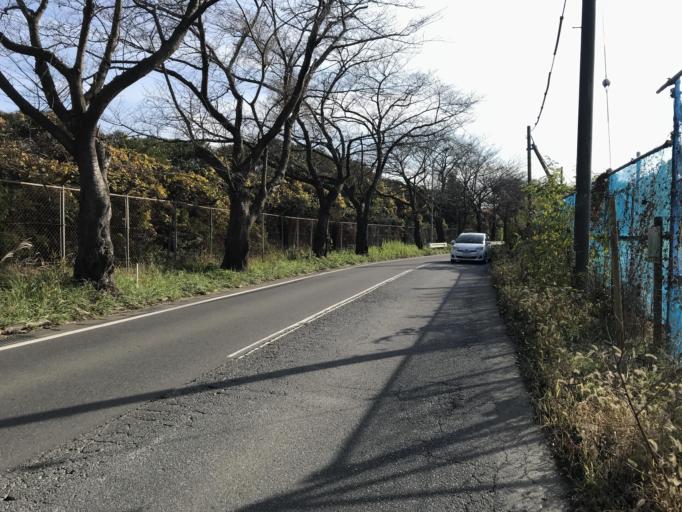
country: JP
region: Chiba
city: Shiroi
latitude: 35.7882
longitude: 140.0103
